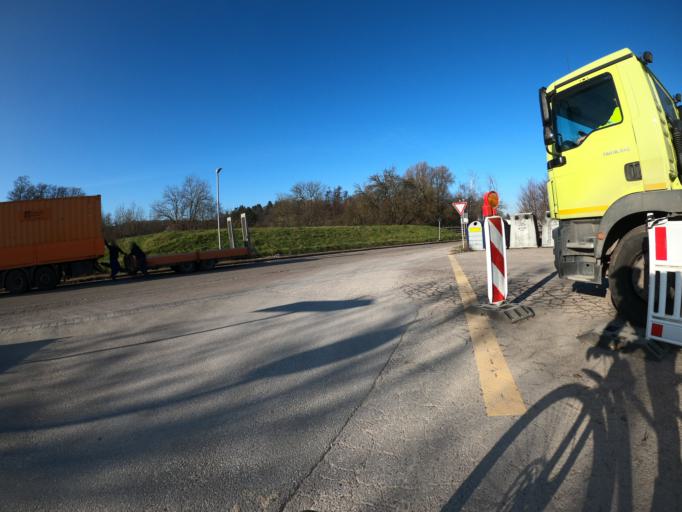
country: DE
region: Baden-Wuerttemberg
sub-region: Regierungsbezirk Stuttgart
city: Goeppingen
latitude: 48.6844
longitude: 9.6711
